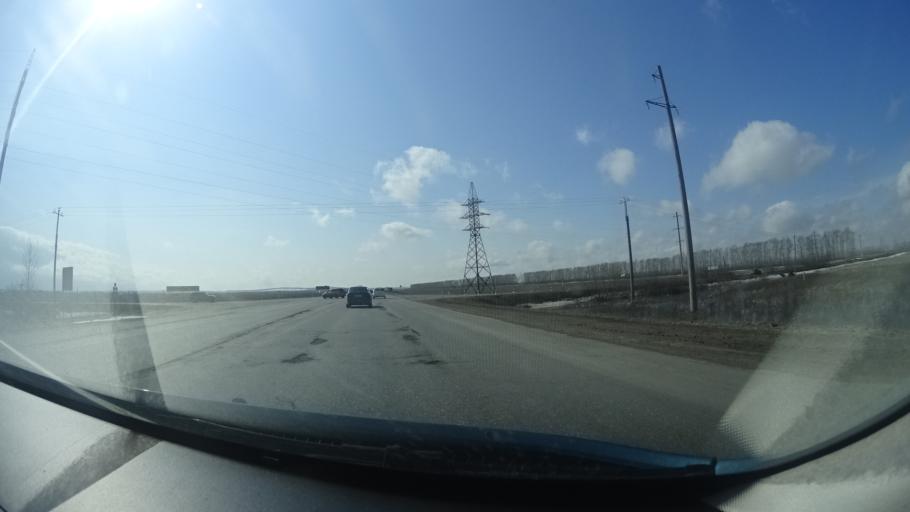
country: RU
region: Bashkortostan
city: Mikhaylovka
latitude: 54.9489
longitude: 55.7524
